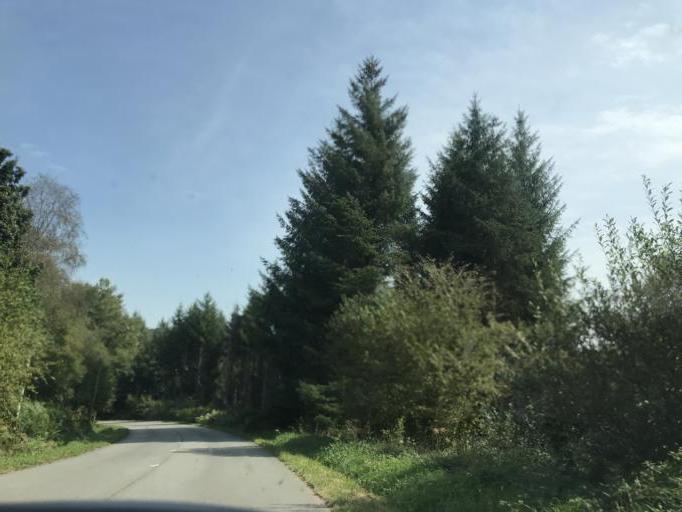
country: FR
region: Brittany
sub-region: Departement du Finistere
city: Loperec
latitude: 48.2942
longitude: -4.0422
